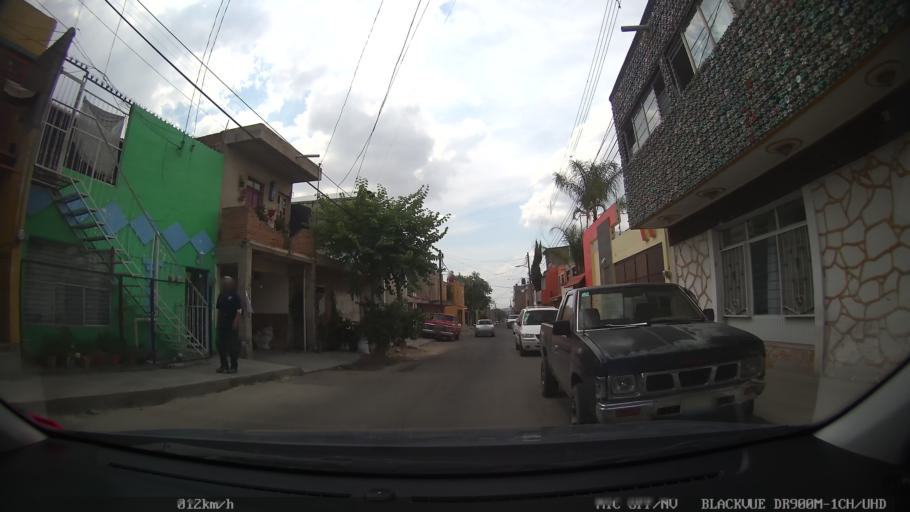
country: MX
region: Jalisco
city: Tonala
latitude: 20.6183
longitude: -103.2428
